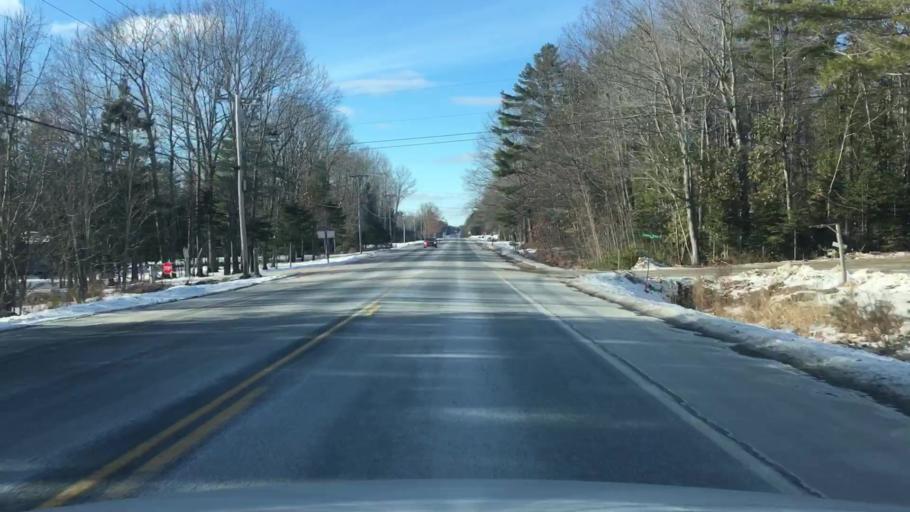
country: US
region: Maine
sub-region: Penobscot County
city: Holden
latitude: 44.8030
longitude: -68.6013
